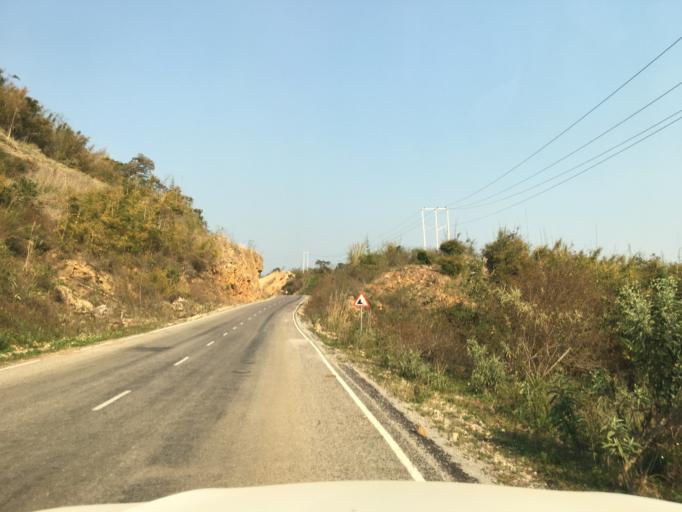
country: LA
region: Houaphan
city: Xam Nua
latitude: 20.5671
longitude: 104.0585
